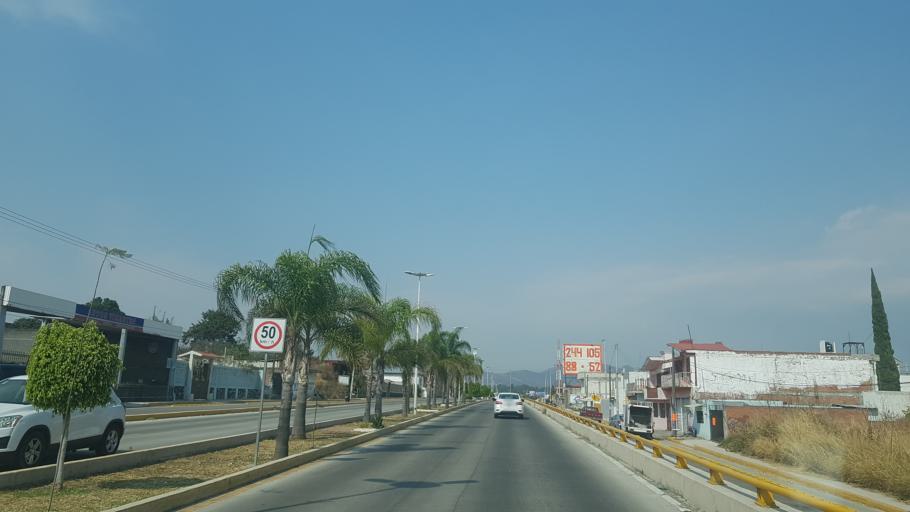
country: MX
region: Puebla
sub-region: Atlixco
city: El Encanto del Cerril
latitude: 18.9216
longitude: -98.4160
